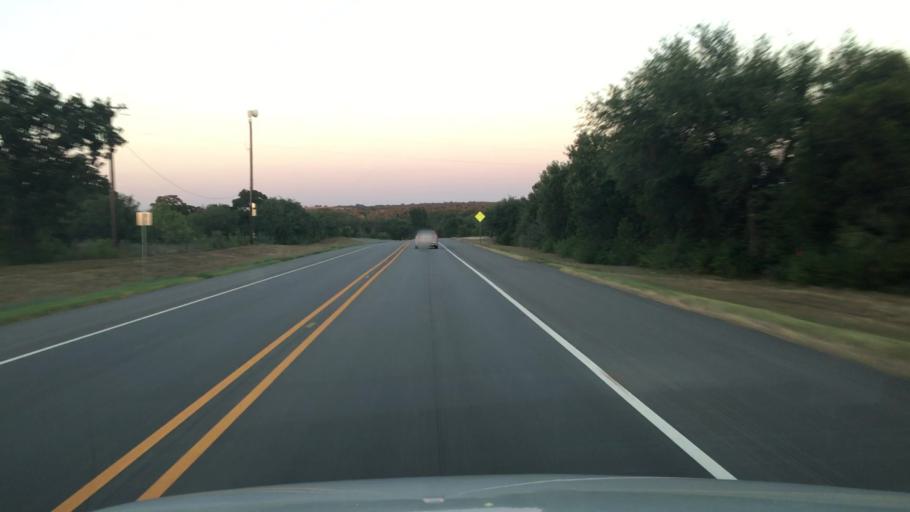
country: US
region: Texas
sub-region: Somervell County
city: Glen Rose
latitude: 32.1911
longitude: -97.8297
